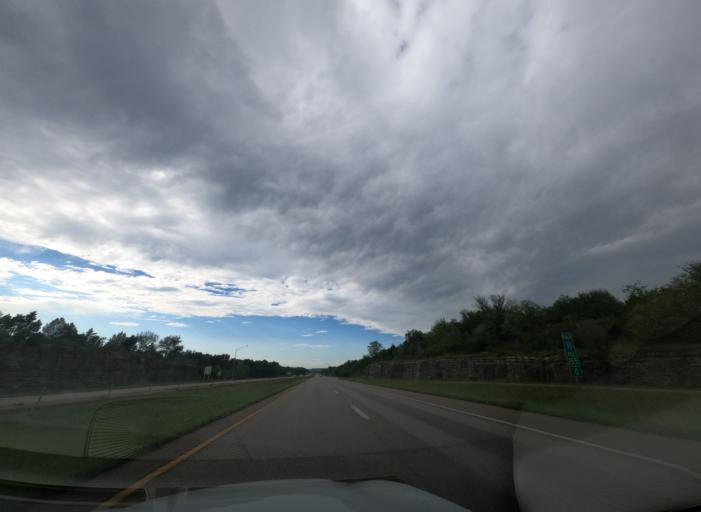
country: US
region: Missouri
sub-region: Sainte Genevieve County
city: Sainte Genevieve
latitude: 37.9759
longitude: -90.1912
